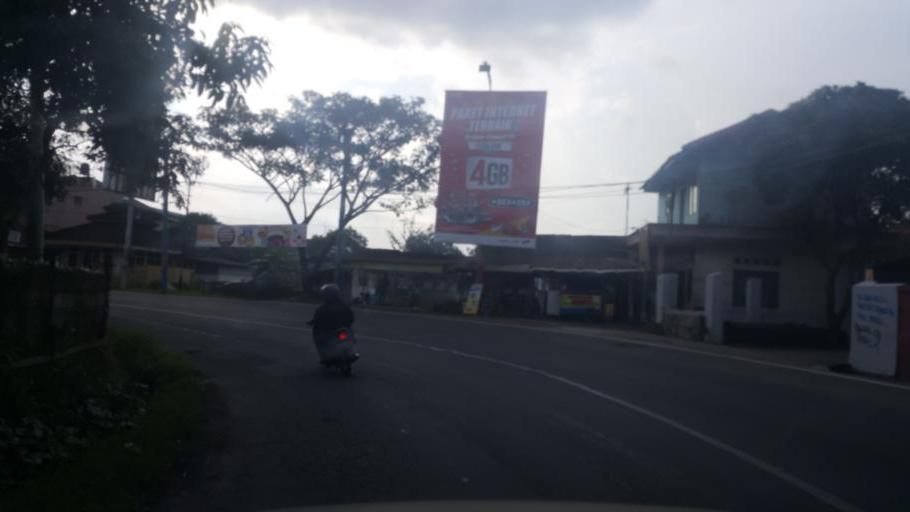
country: ID
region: West Java
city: Cibogor
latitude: -7.3142
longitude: 108.2288
